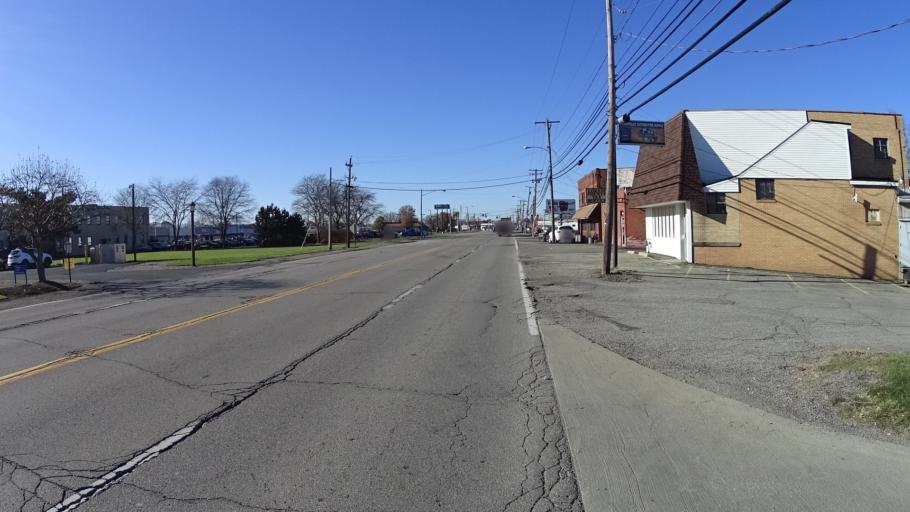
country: US
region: Ohio
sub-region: Lorain County
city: Elyria
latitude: 41.3791
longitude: -82.0718
